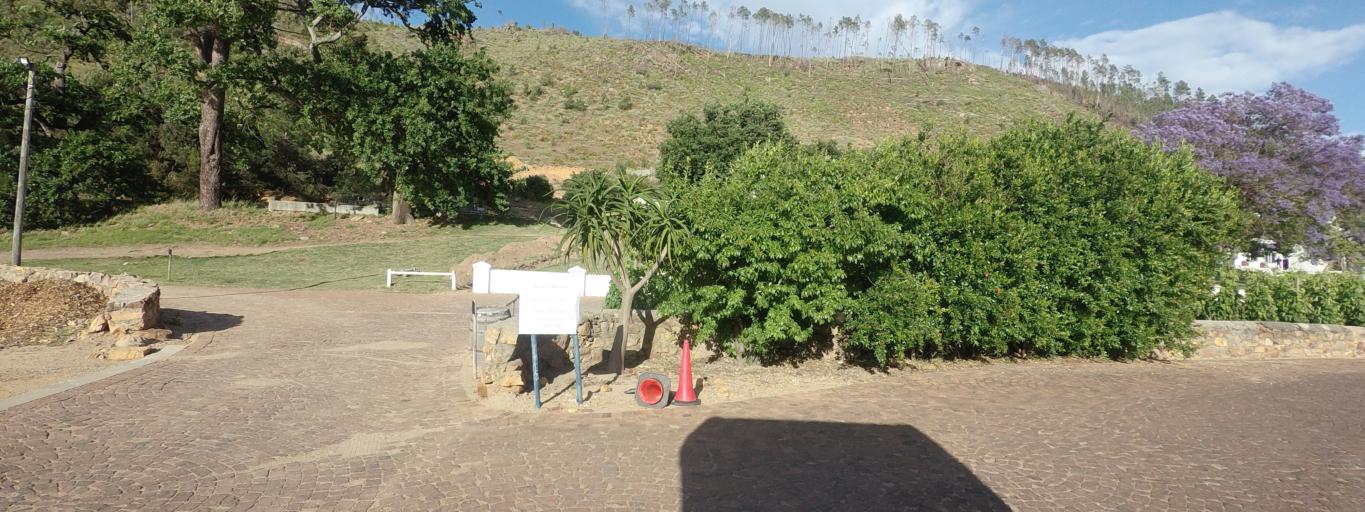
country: ZA
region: Western Cape
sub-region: Cape Winelands District Municipality
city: Paarl
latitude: -33.9002
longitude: 19.0920
